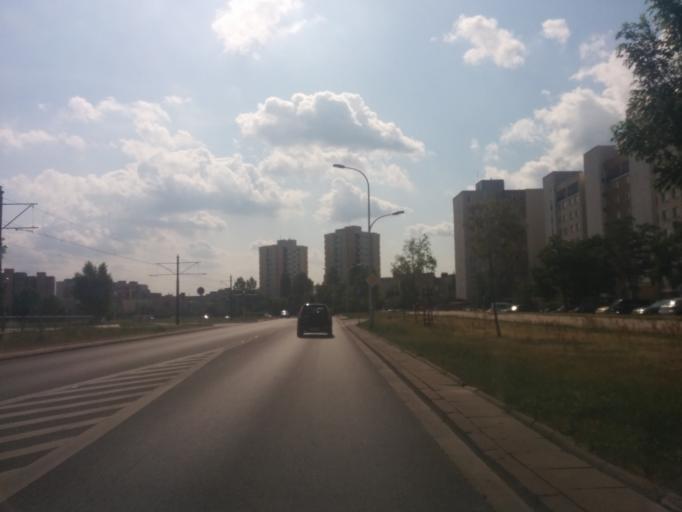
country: PL
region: Masovian Voivodeship
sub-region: Warszawa
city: Bialoleka
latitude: 52.3175
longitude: 20.9544
